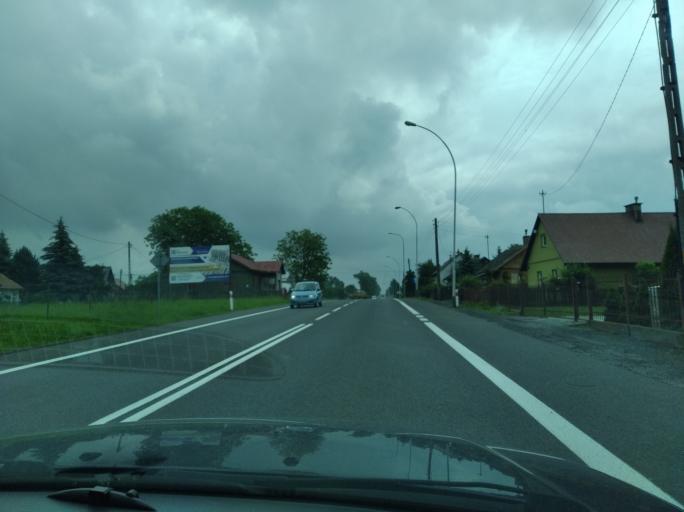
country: PL
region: Subcarpathian Voivodeship
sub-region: Powiat przeworski
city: Przeworsk
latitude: 50.0554
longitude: 22.5089
